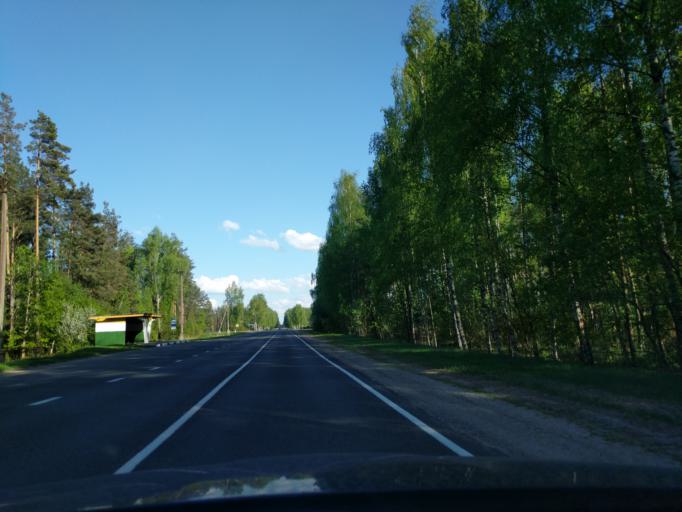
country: BY
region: Minsk
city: Myadzyel
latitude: 54.8162
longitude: 26.9680
